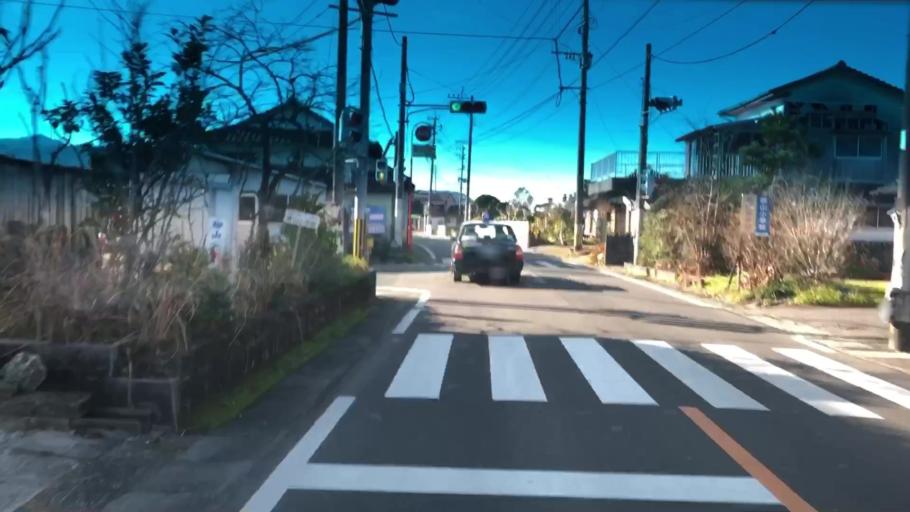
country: JP
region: Kagoshima
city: Satsumasendai
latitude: 31.8240
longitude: 130.2540
